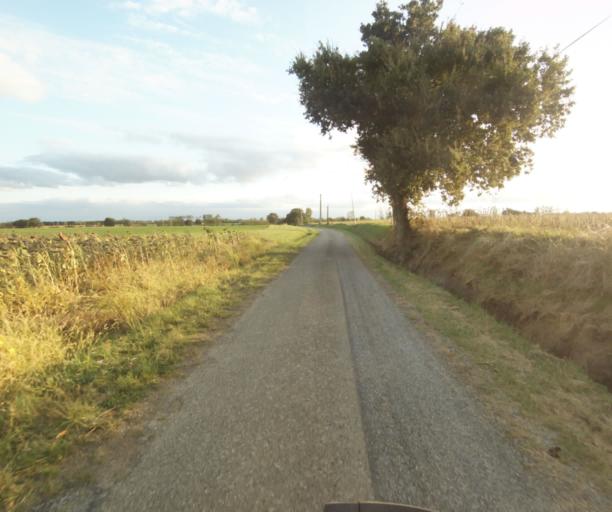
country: FR
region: Midi-Pyrenees
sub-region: Departement de la Haute-Garonne
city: Launac
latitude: 43.8074
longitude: 1.1635
